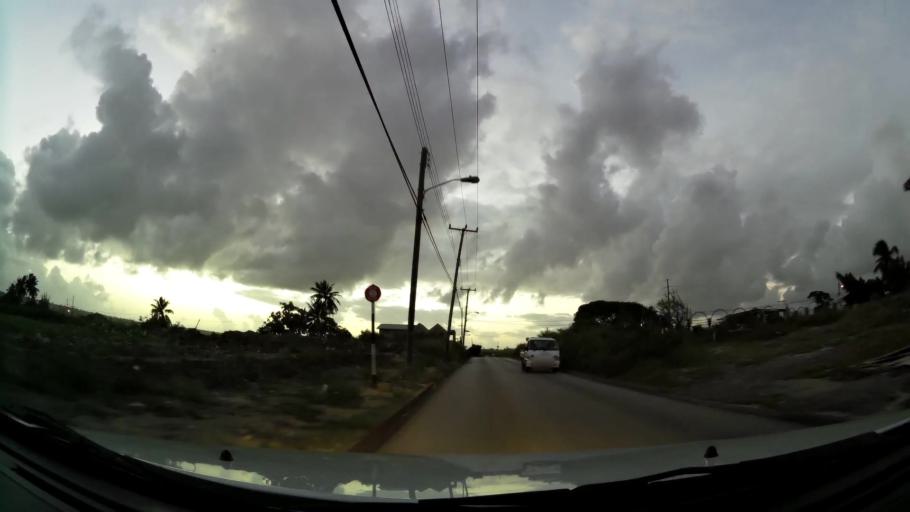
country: BB
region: Saint Philip
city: Crane
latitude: 13.1186
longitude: -59.4833
